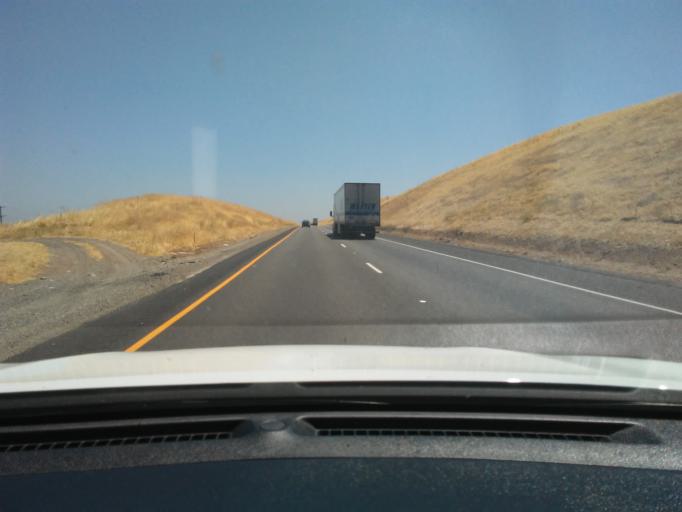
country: US
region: California
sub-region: Stanislaus County
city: Patterson
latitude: 37.4473
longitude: -121.1687
